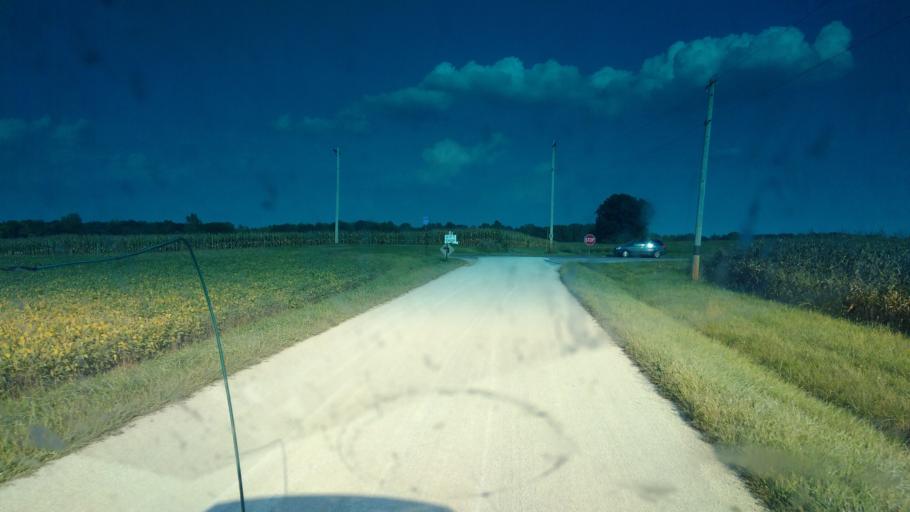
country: US
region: Ohio
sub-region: Wyandot County
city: Upper Sandusky
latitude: 40.9354
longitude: -83.1322
